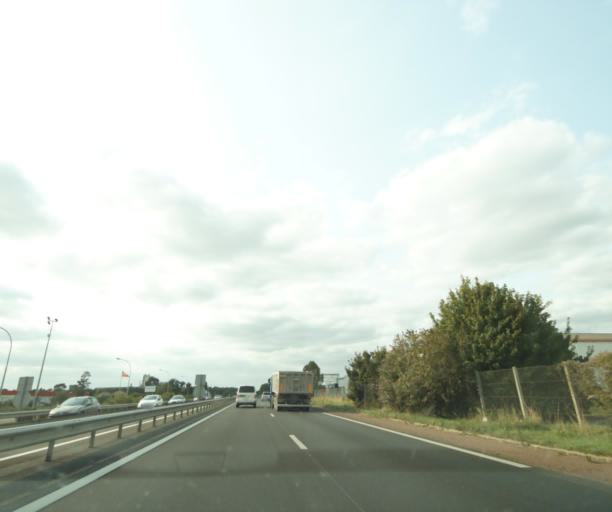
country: FR
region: Centre
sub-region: Departement d'Indre-et-Loire
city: Esvres
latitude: 47.3009
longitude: 0.7969
